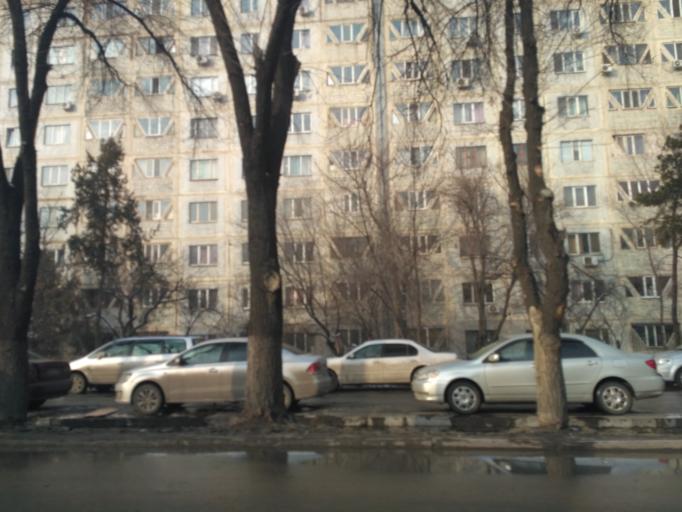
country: KZ
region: Almaty Qalasy
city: Almaty
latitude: 43.2397
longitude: 76.8316
